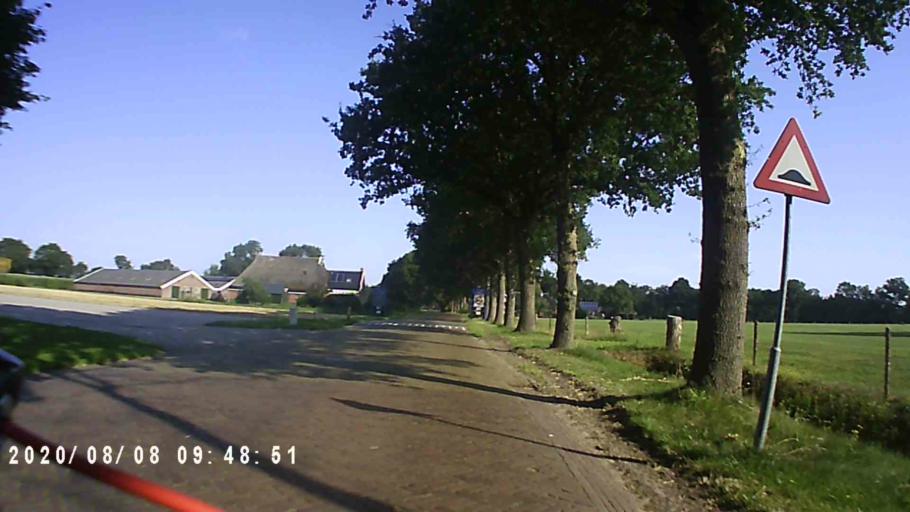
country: NL
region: Groningen
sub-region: Gemeente Leek
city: Leek
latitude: 53.0800
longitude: 6.3925
